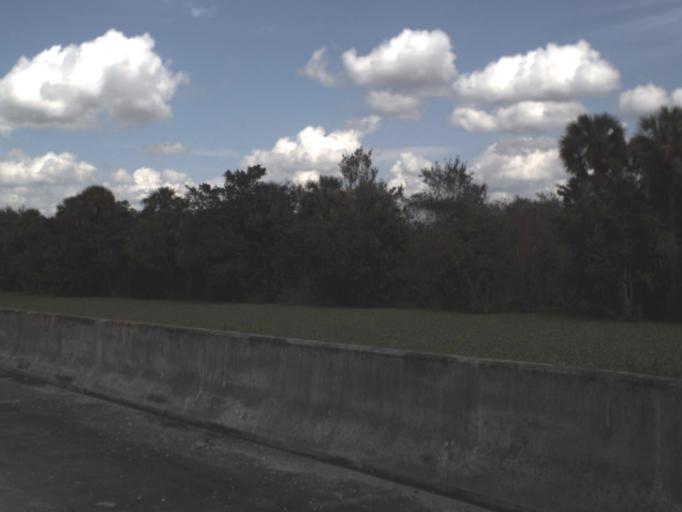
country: US
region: Florida
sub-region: Collier County
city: Immokalee
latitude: 26.2036
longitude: -81.3462
